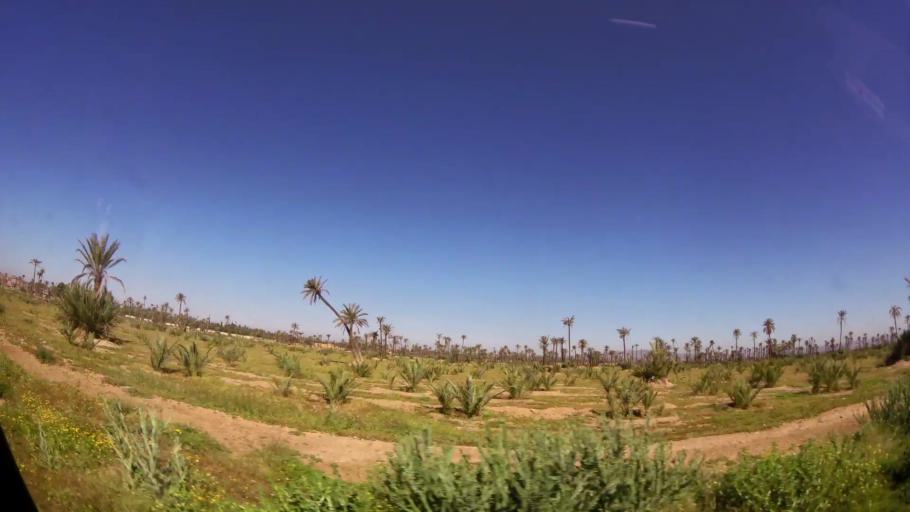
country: MA
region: Marrakech-Tensift-Al Haouz
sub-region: Marrakech
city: Marrakesh
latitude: 31.6585
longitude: -7.9500
